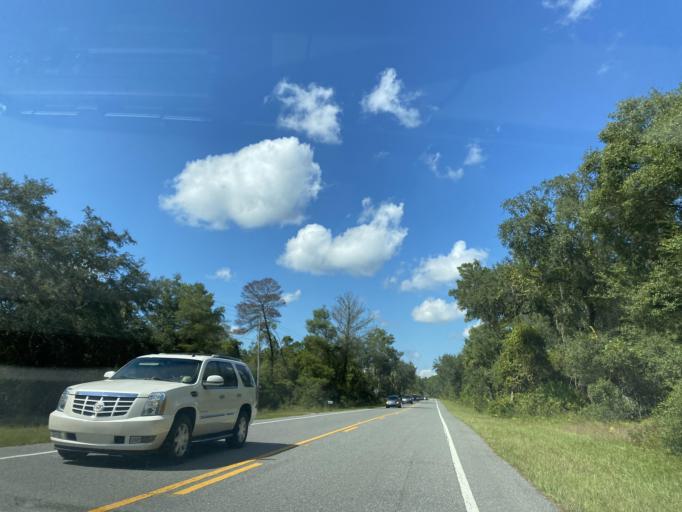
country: US
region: Florida
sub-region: Lake County
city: Lake Mack-Forest Hills
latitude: 29.0103
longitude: -81.4570
